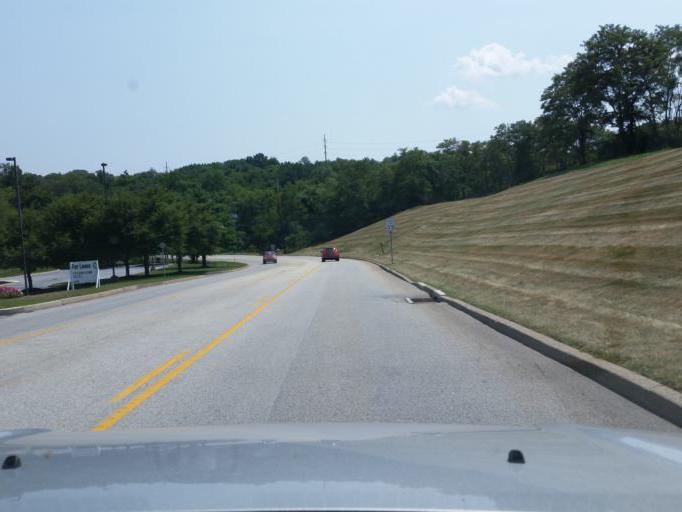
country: US
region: Pennsylvania
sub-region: Dauphin County
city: Lawnton
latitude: 40.2703
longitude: -76.8130
